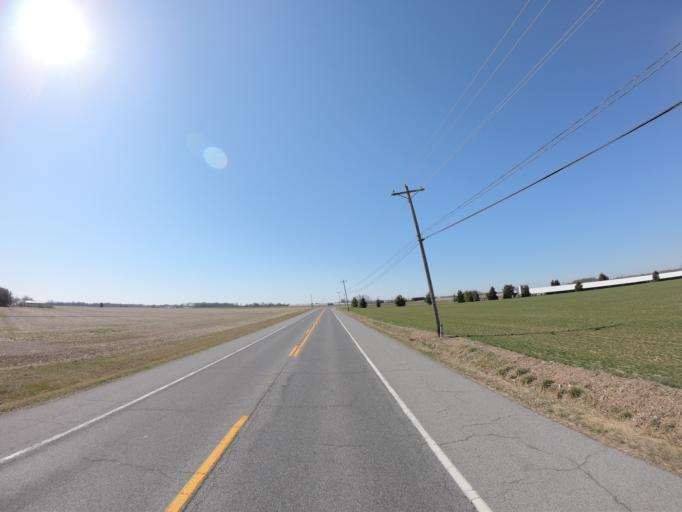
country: US
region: Maryland
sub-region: Queen Anne's County
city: Kingstown
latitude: 39.3240
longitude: -75.9638
